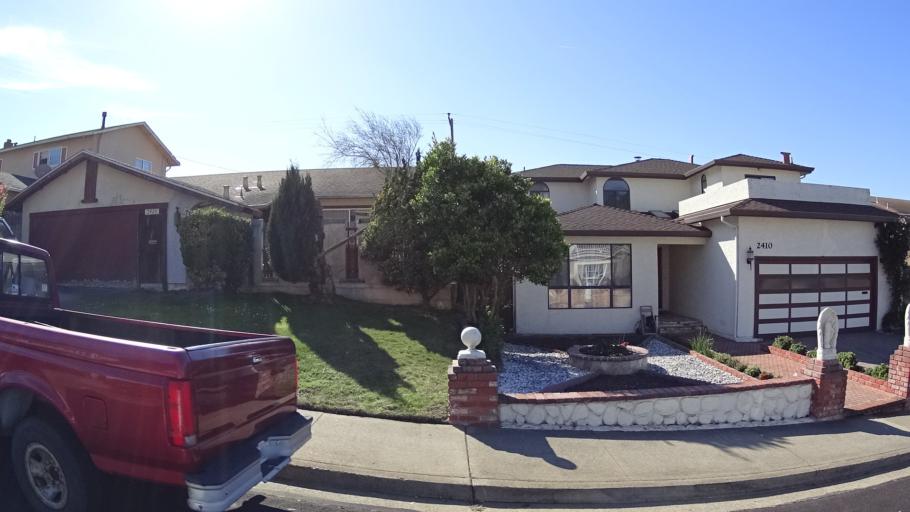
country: US
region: California
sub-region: San Mateo County
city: Colma
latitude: 37.6398
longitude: -122.4511
